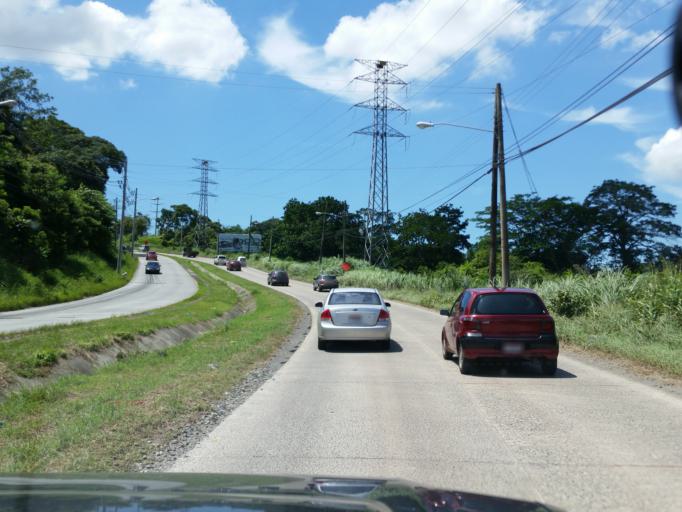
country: PA
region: Panama
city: San Miguelito
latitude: 9.0674
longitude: -79.4629
